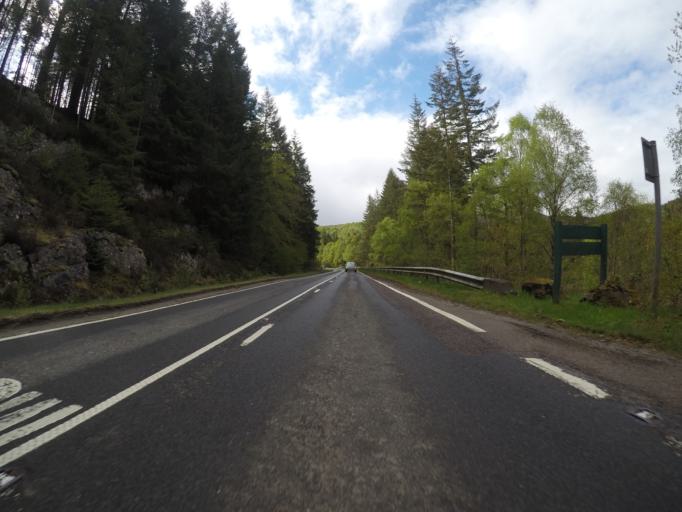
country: GB
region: Scotland
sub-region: Highland
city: Spean Bridge
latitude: 57.0688
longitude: -4.8319
